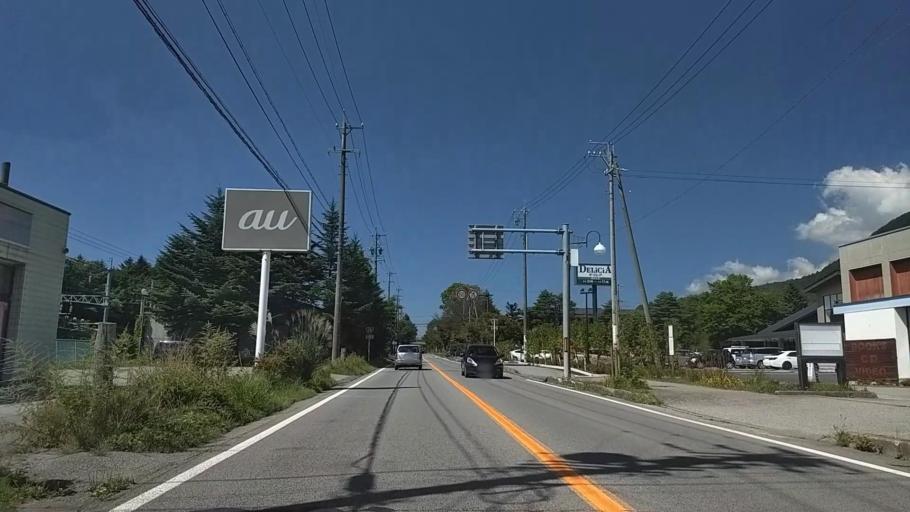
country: JP
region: Nagano
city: Saku
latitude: 36.3435
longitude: 138.6258
